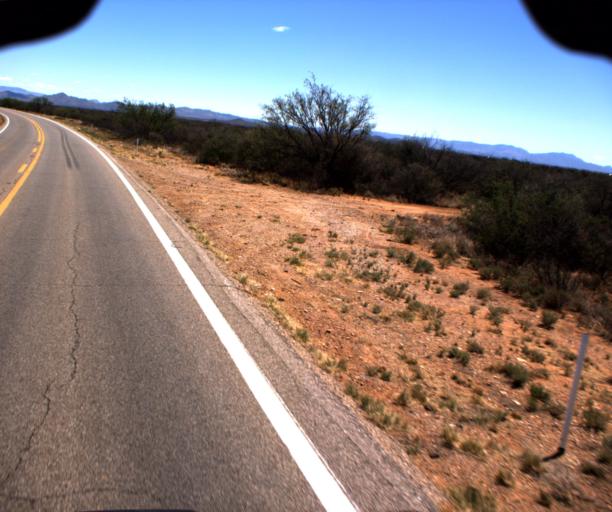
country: US
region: Arizona
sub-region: Cochise County
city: Huachuca City
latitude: 31.6935
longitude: -110.3165
